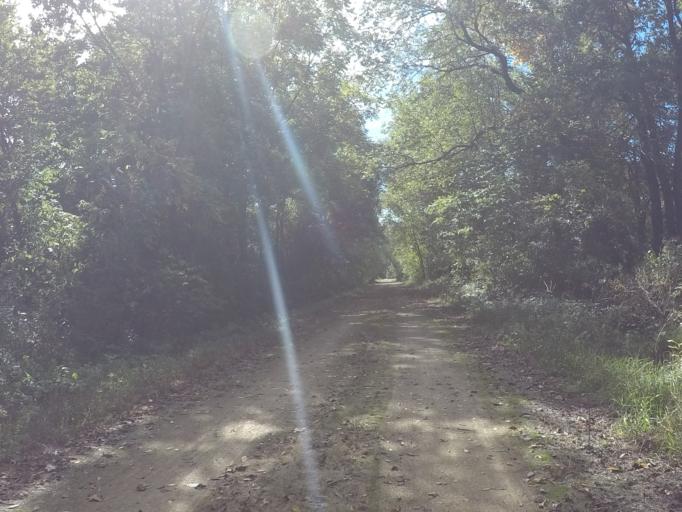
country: US
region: Wisconsin
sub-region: Richland County
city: Richland Center
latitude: 43.2253
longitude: -90.2976
